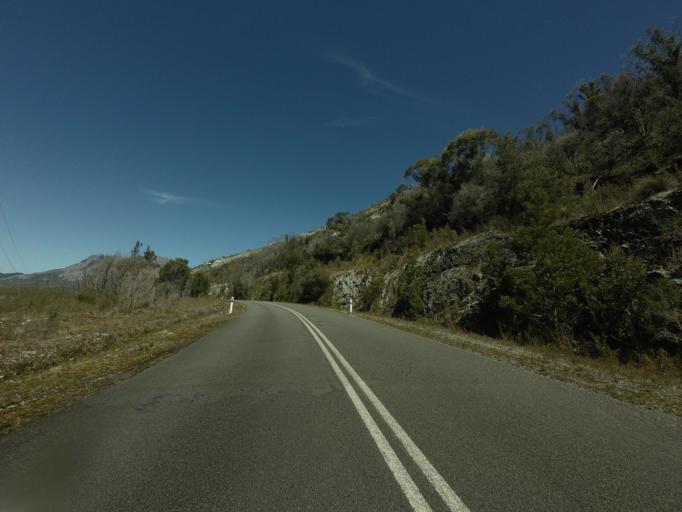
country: AU
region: Tasmania
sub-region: Huon Valley
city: Geeveston
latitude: -42.8509
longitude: 146.1817
